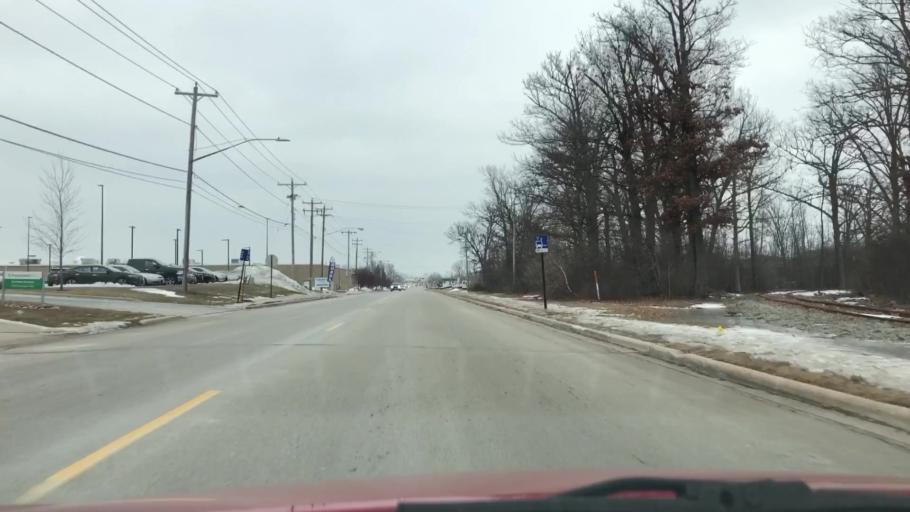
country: US
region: Wisconsin
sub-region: Brown County
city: Ashwaubenon
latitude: 44.4709
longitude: -88.0724
